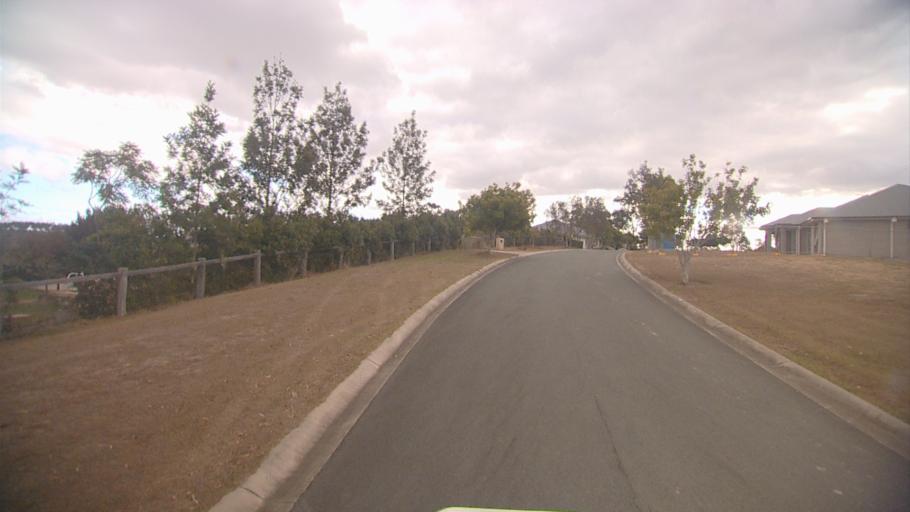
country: AU
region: Queensland
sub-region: Logan
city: Cedar Vale
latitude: -27.8713
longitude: 153.0724
